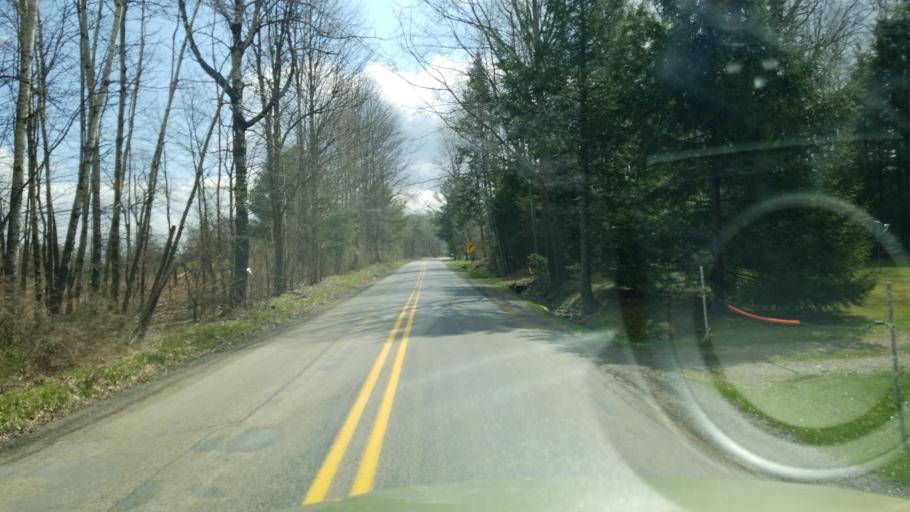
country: US
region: Pennsylvania
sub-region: Jefferson County
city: Brockway
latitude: 41.2788
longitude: -78.8461
